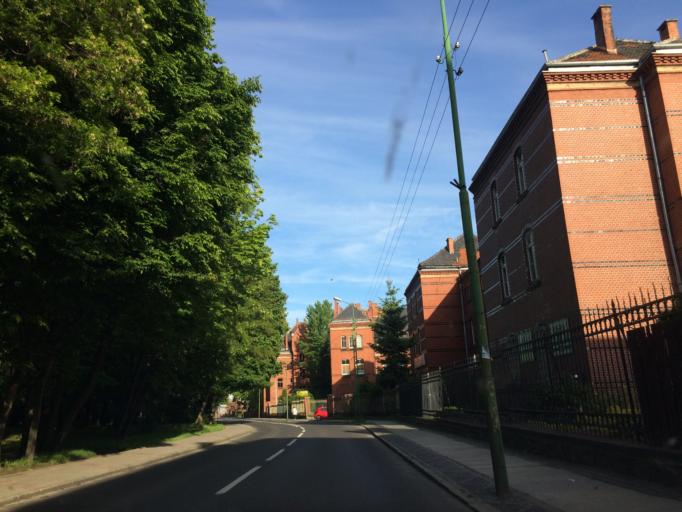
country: PL
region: Lower Silesian Voivodeship
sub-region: Powiat swidnicki
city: Swidnica
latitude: 50.8393
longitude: 16.4775
